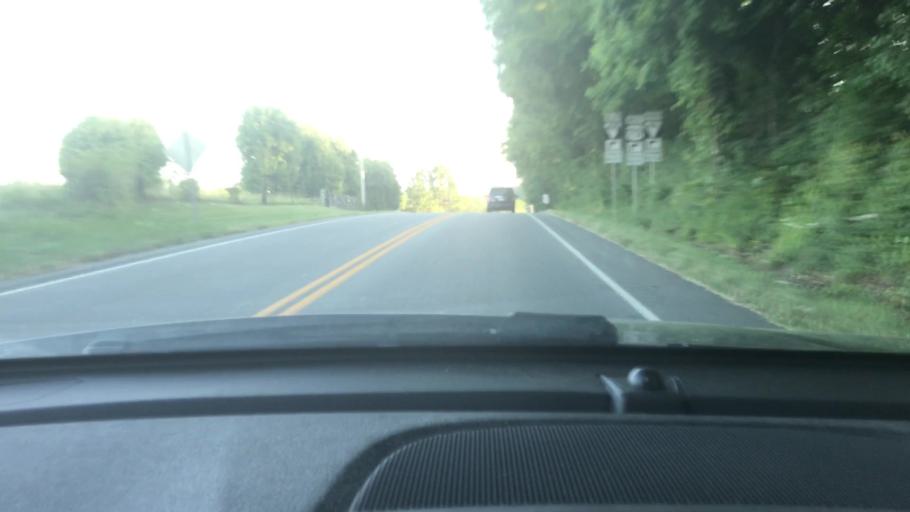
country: US
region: Tennessee
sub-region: Dickson County
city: Dickson
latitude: 36.0882
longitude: -87.3775
